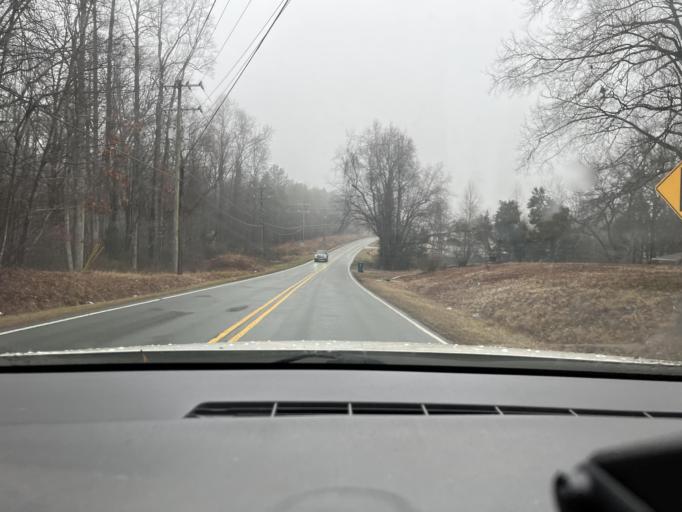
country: US
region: North Carolina
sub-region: Guilford County
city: Pleasant Garden
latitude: 35.9877
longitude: -79.7778
